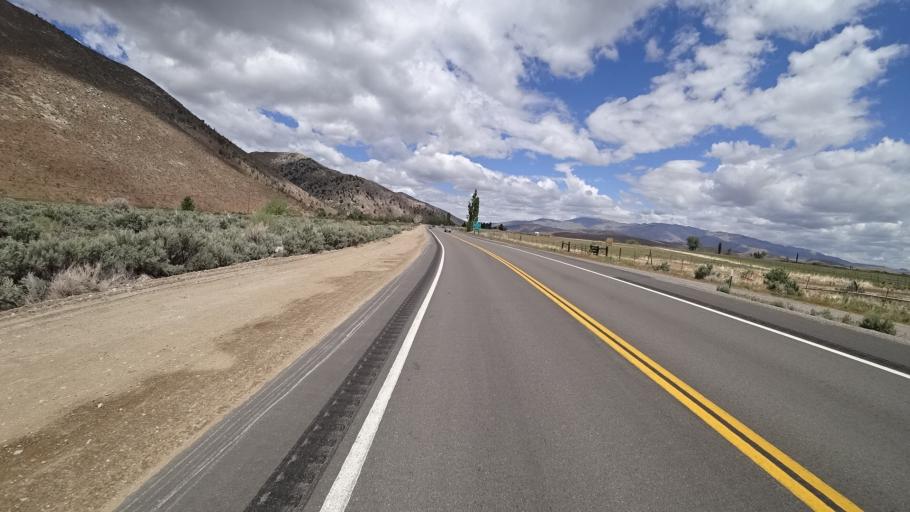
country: US
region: Nevada
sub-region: Lyon County
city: Smith Valley
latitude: 38.6352
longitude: -119.5243
